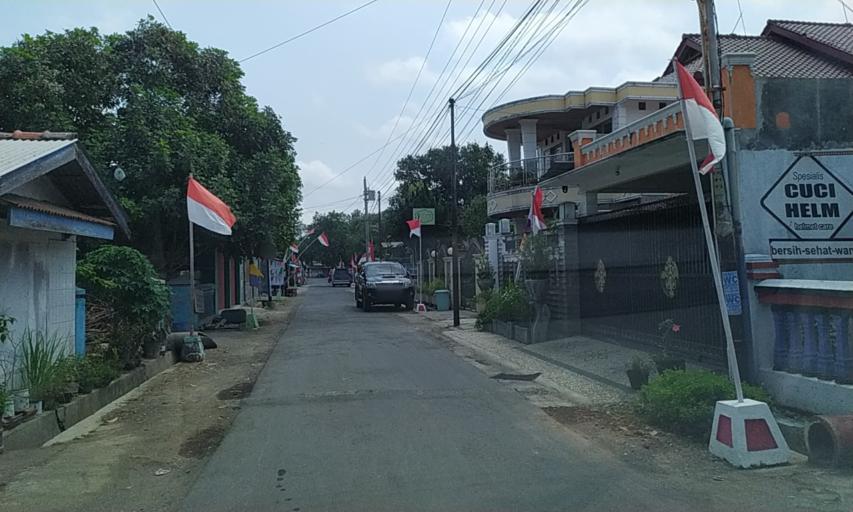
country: ID
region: Central Java
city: Karangbadar Kidul
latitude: -7.7353
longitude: 109.0160
